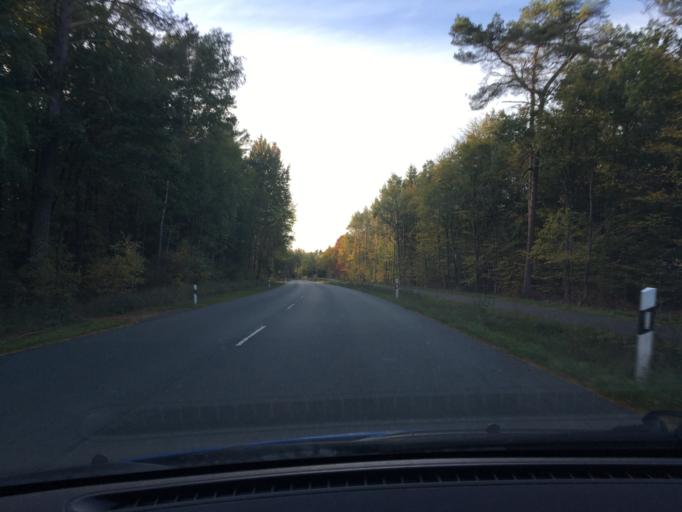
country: DE
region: Lower Saxony
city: Munster
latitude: 53.0438
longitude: 10.0564
